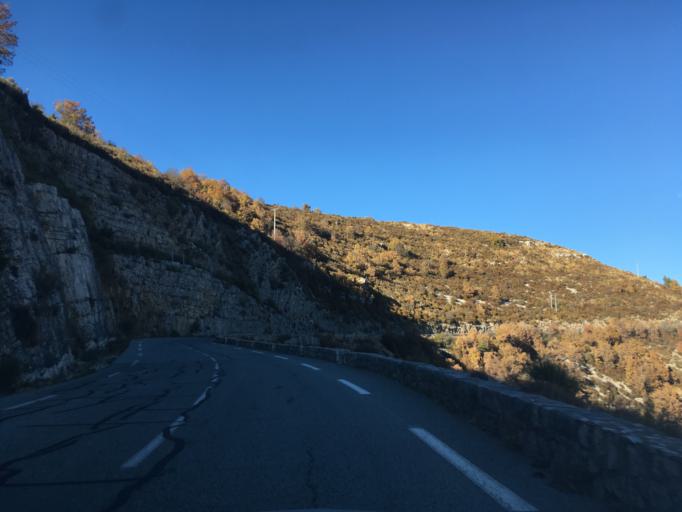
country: FR
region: Provence-Alpes-Cote d'Azur
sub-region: Departement du Var
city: Montferrat
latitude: 43.6773
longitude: 6.5072
